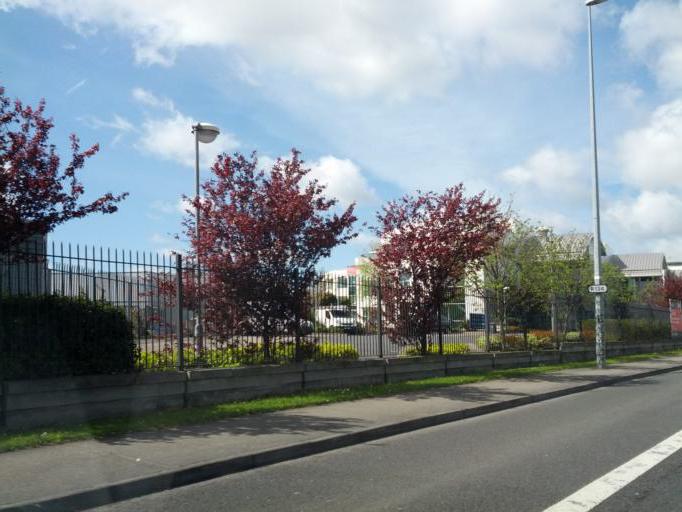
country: IE
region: Leinster
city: Ballyfermot
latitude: 53.3264
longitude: -6.3608
